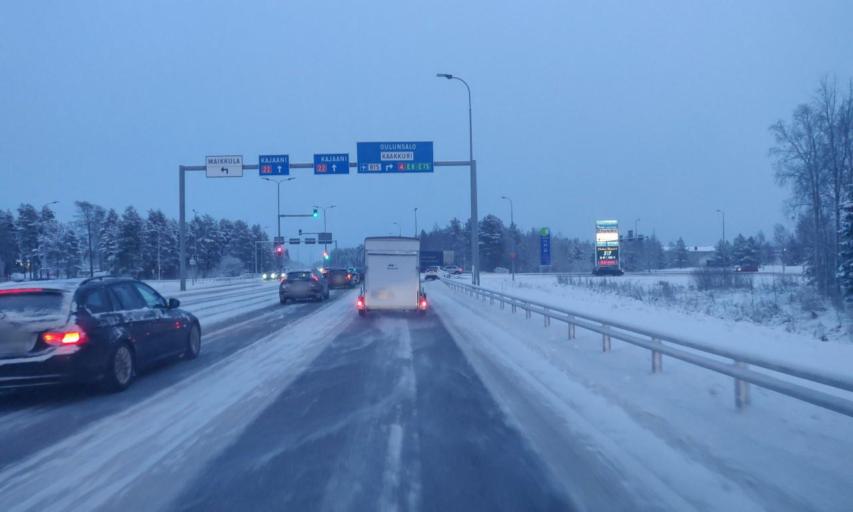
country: FI
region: Northern Ostrobothnia
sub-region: Oulu
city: Kempele
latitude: 64.9811
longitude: 25.5593
